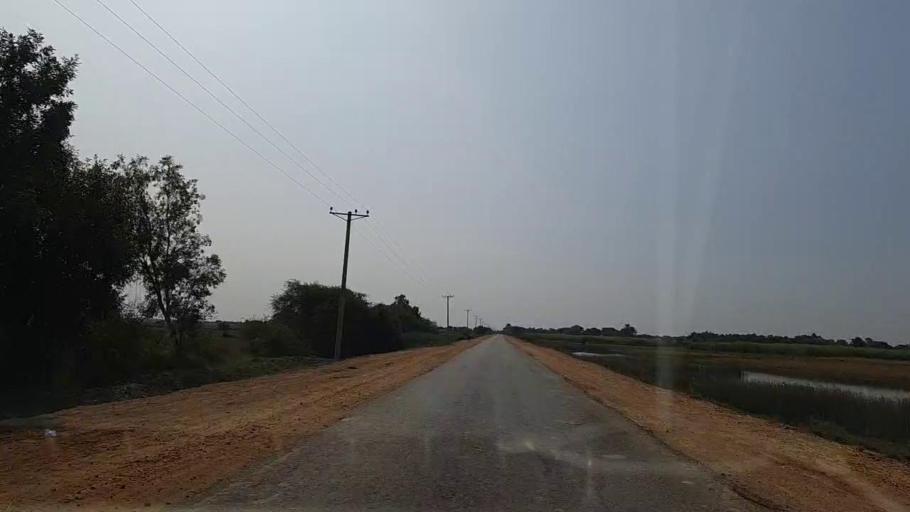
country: PK
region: Sindh
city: Chuhar Jamali
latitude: 24.3573
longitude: 67.9578
